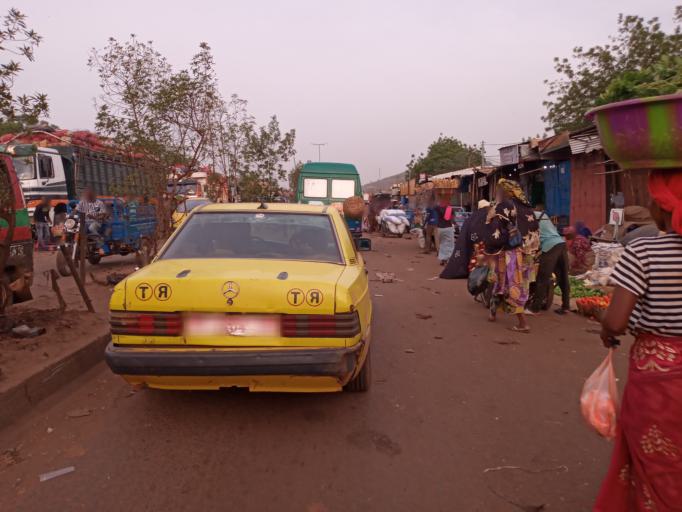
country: ML
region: Bamako
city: Bamako
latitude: 12.6591
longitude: -7.9863
